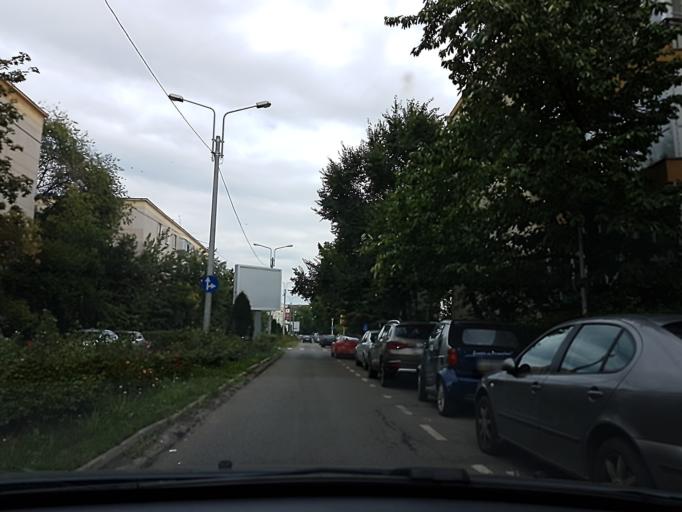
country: RO
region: Bucuresti
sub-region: Municipiul Bucuresti
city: Bucharest
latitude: 44.4636
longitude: 26.1019
